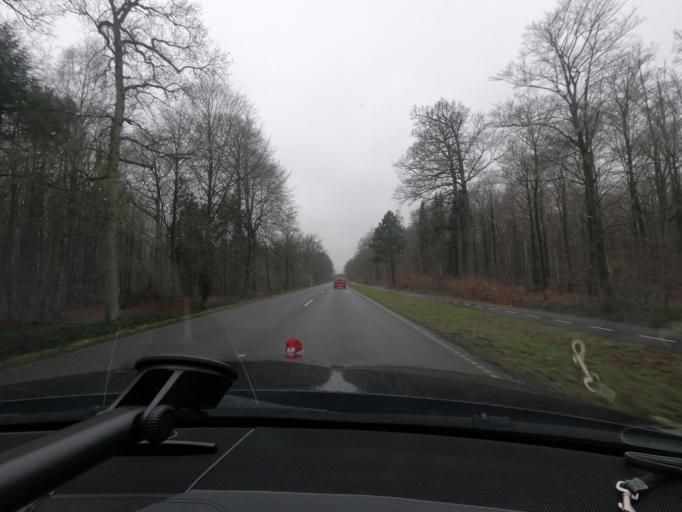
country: DK
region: South Denmark
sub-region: Sonderborg Kommune
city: Sonderborg
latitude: 54.9065
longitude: 9.8320
